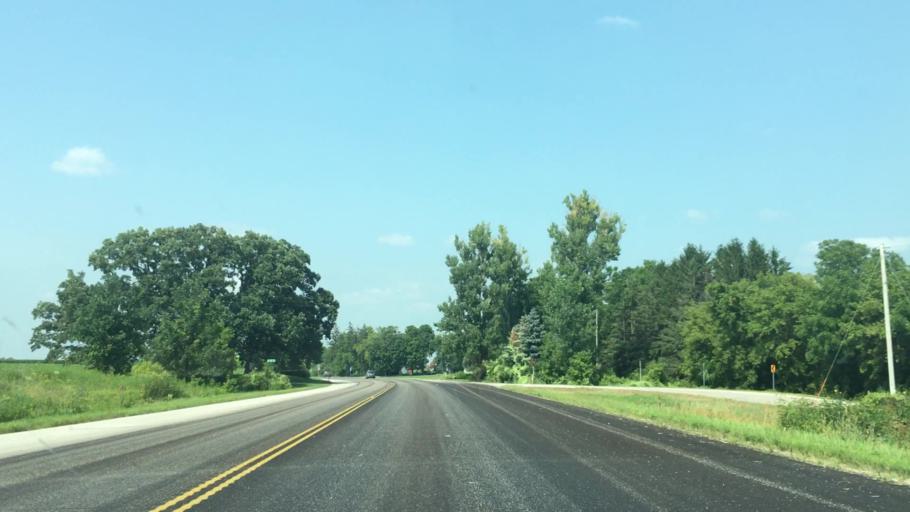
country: US
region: Minnesota
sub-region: Fillmore County
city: Harmony
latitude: 43.5093
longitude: -91.8703
